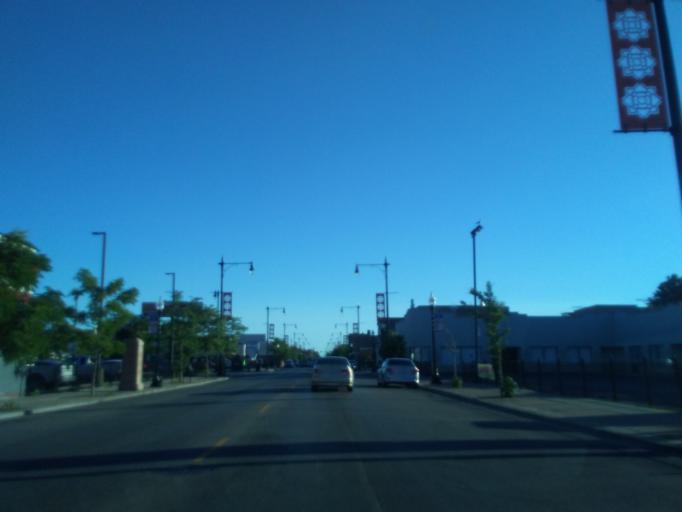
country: US
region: Illinois
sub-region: Cook County
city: Lincolnwood
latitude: 41.9619
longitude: -87.7278
